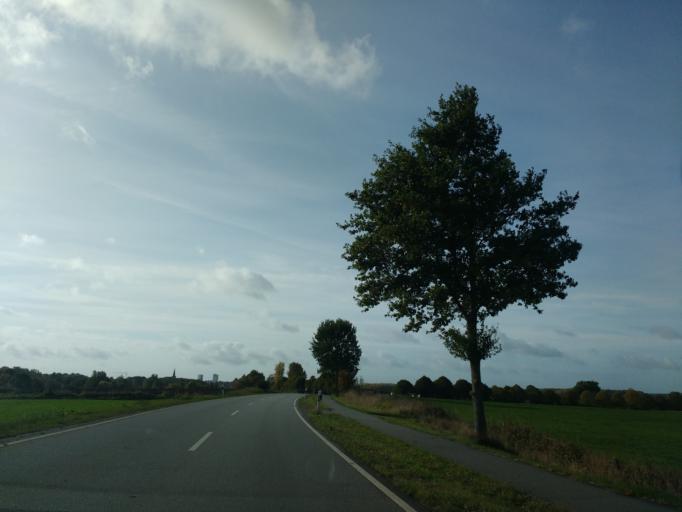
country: DE
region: Schleswig-Holstein
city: Altenkrempe
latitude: 54.1231
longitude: 10.8222
